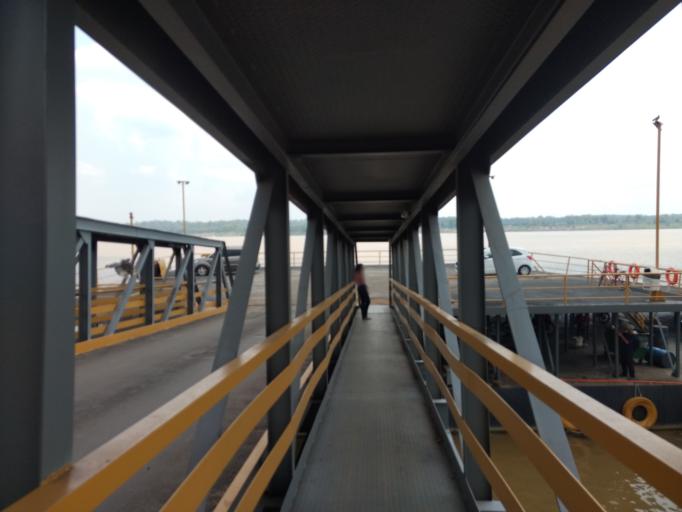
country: BR
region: Rondonia
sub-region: Porto Velho
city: Porto Velho
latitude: -8.7700
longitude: -63.9099
